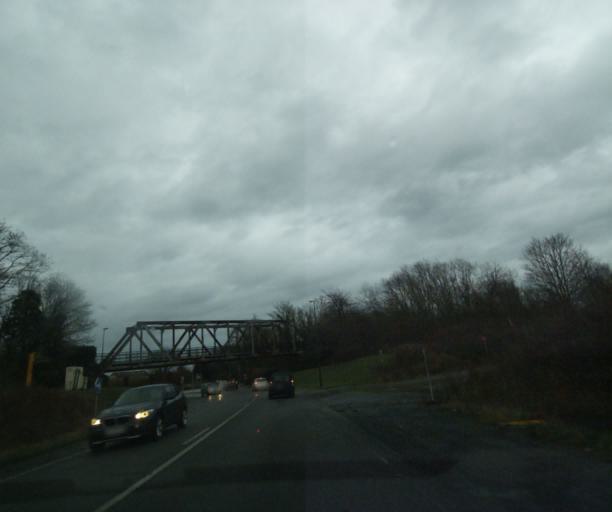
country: FR
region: Nord-Pas-de-Calais
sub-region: Departement du Nord
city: Conde-sur-l'Escaut
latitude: 50.4468
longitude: 3.5842
